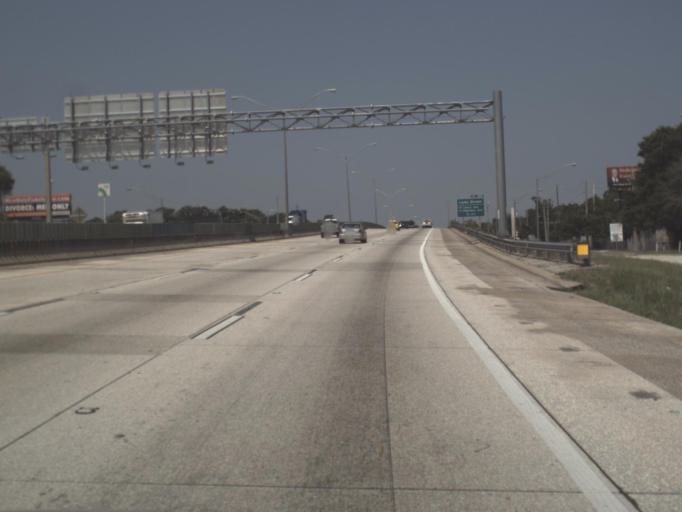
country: US
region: Florida
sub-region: Duval County
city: Jacksonville
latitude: 30.3211
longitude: -81.7027
